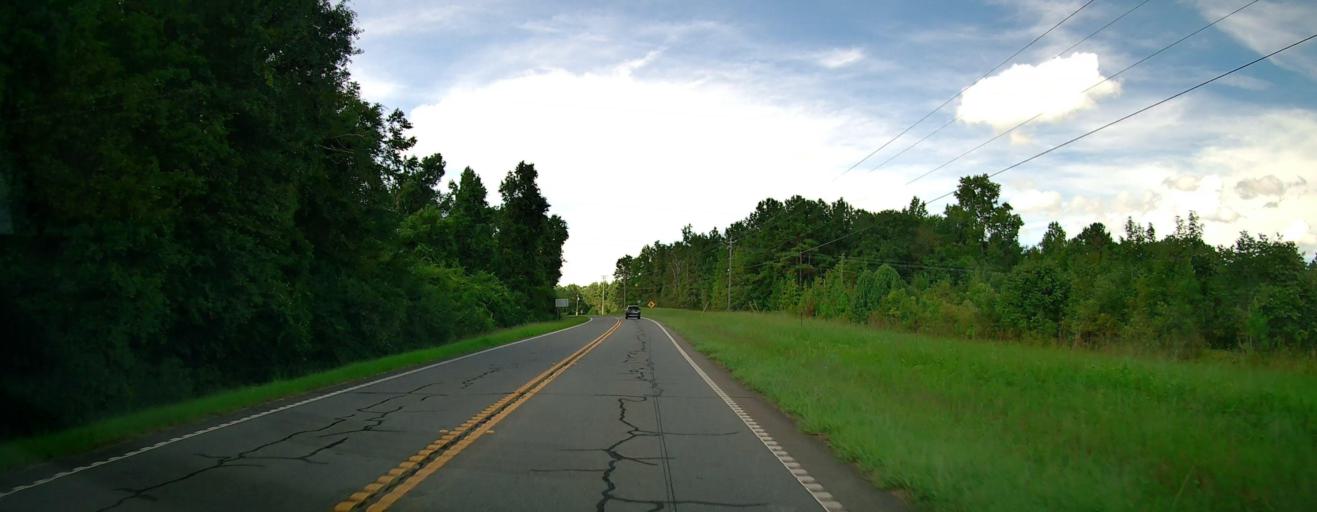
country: US
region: Georgia
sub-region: Talbot County
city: Sardis
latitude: 32.7754
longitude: -84.5578
